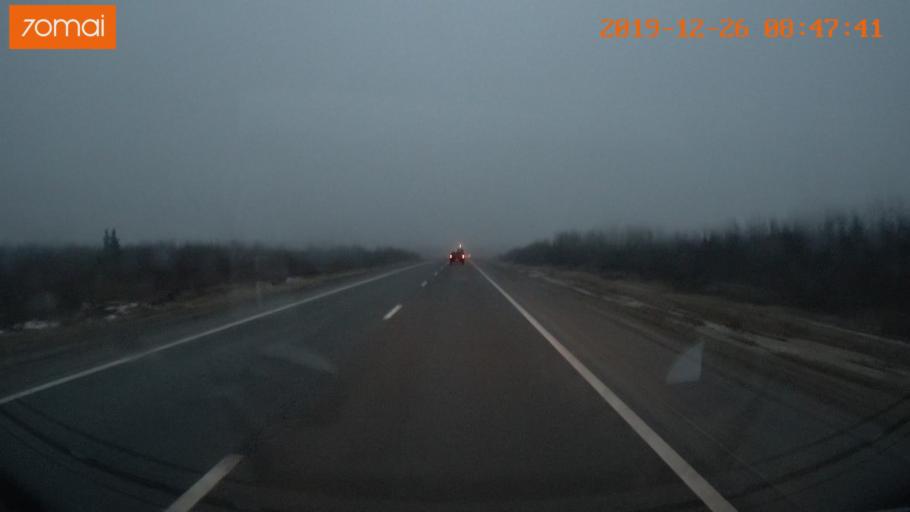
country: RU
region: Jaroslavl
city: Prechistoye
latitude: 58.6262
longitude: 40.3301
